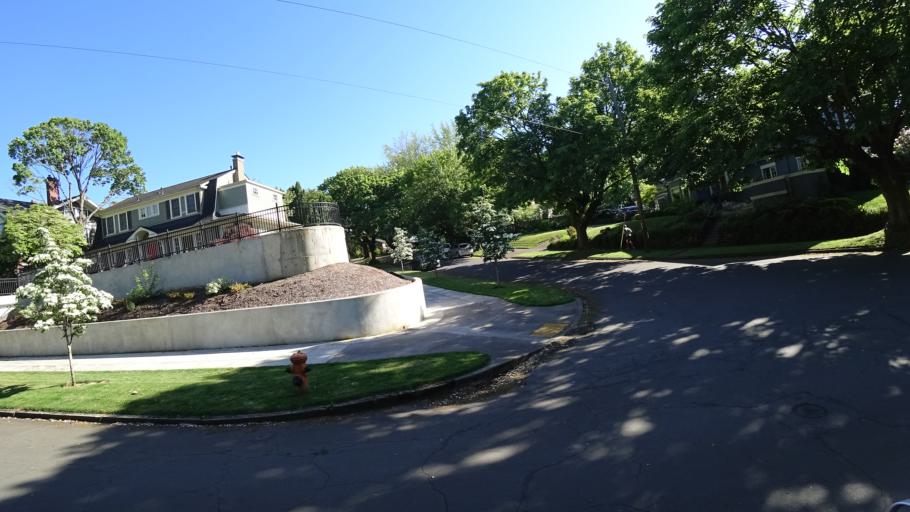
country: US
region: Oregon
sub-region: Multnomah County
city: Portland
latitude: 45.5251
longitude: -122.6286
